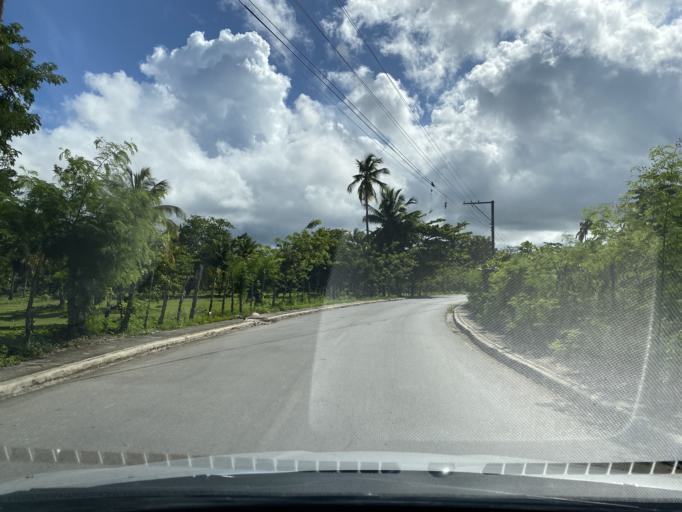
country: DO
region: Samana
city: Las Terrenas
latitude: 19.3243
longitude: -69.5292
